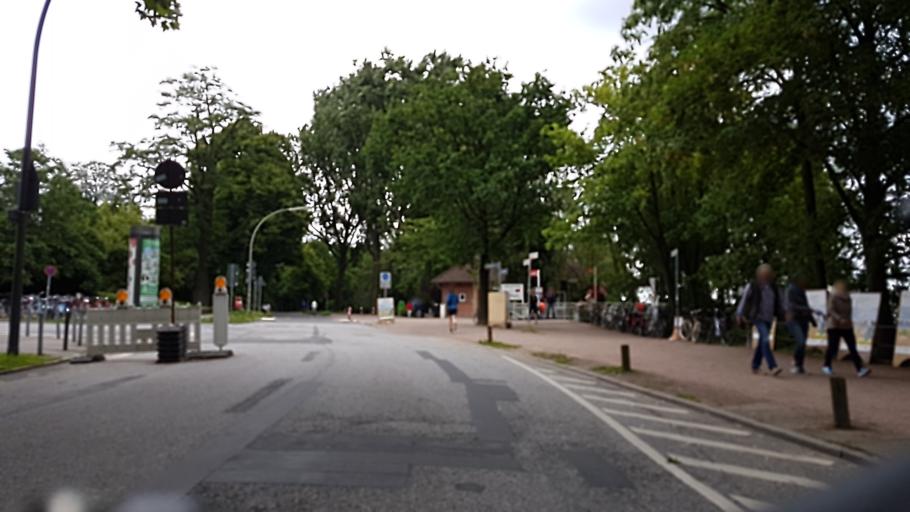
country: DE
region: Hamburg
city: St. Georg
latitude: 53.5670
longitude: 10.0012
